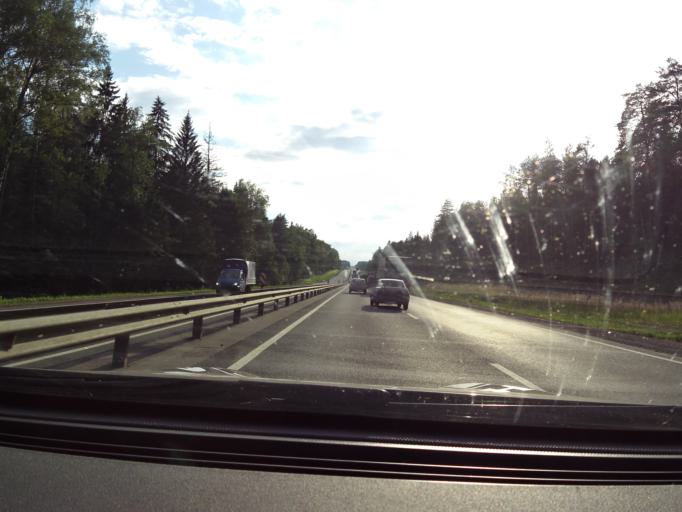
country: RU
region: Vladimir
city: Kameshkovo
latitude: 56.1978
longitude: 41.0243
